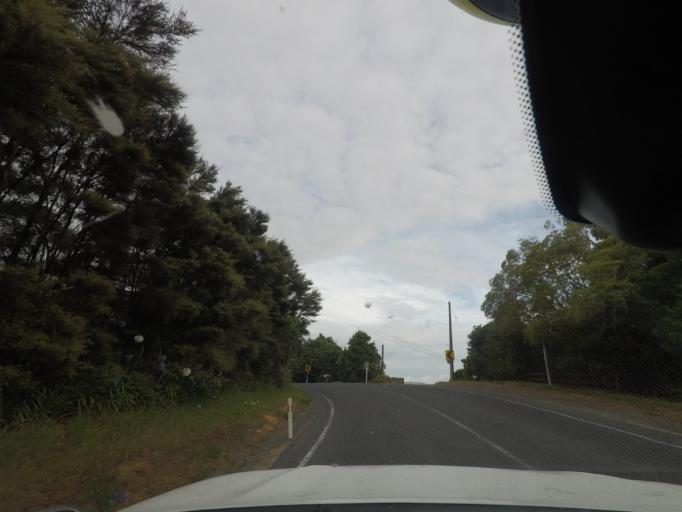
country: NZ
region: Auckland
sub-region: Auckland
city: Parakai
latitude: -36.5277
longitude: 174.2935
